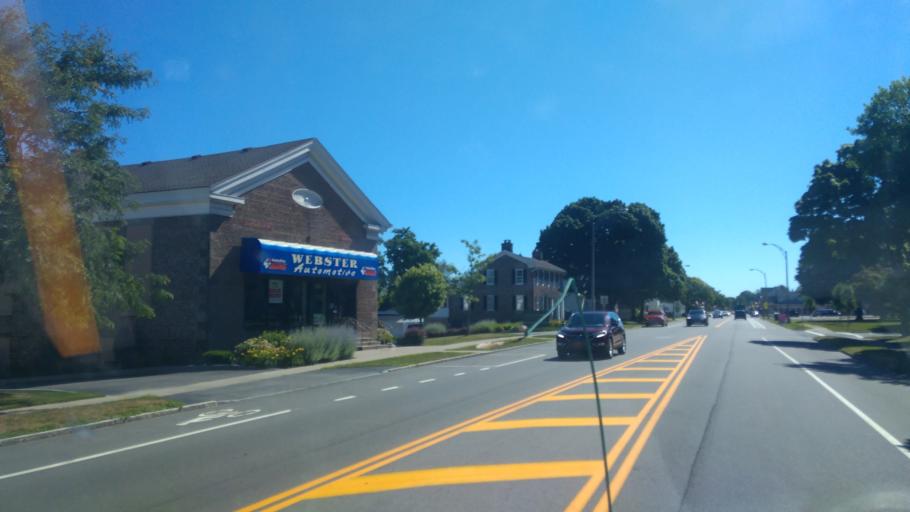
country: US
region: New York
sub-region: Monroe County
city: Webster
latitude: 43.2117
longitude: -77.4349
